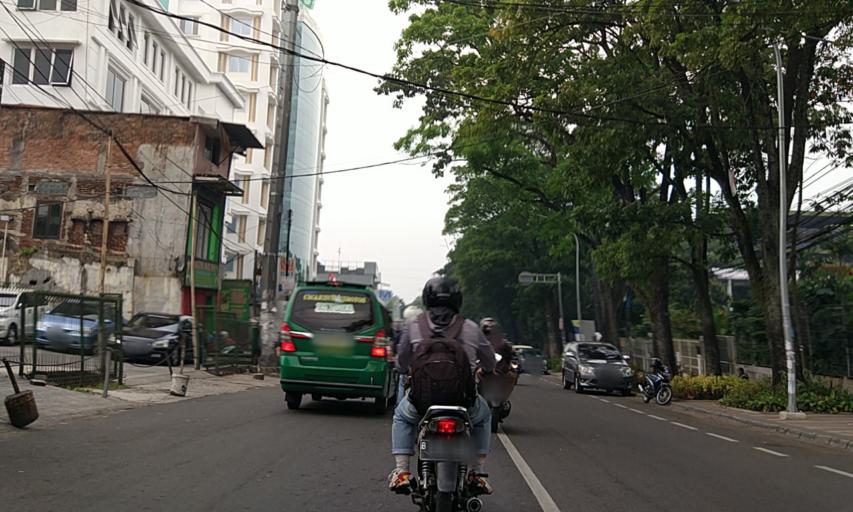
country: ID
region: West Java
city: Bandung
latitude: -6.8864
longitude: 107.6149
